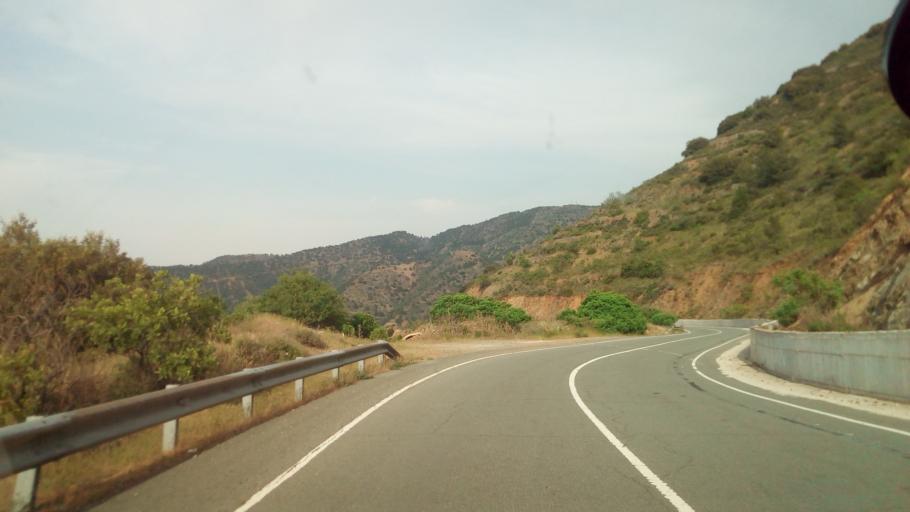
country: CY
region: Lefkosia
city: Kakopetria
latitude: 35.0038
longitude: 32.8131
